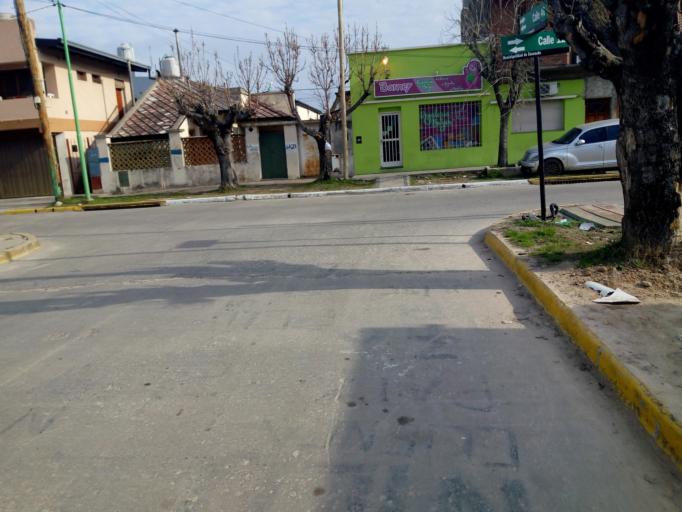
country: AR
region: Buenos Aires
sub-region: Partido de La Plata
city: La Plata
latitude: -34.8966
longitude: -57.9374
